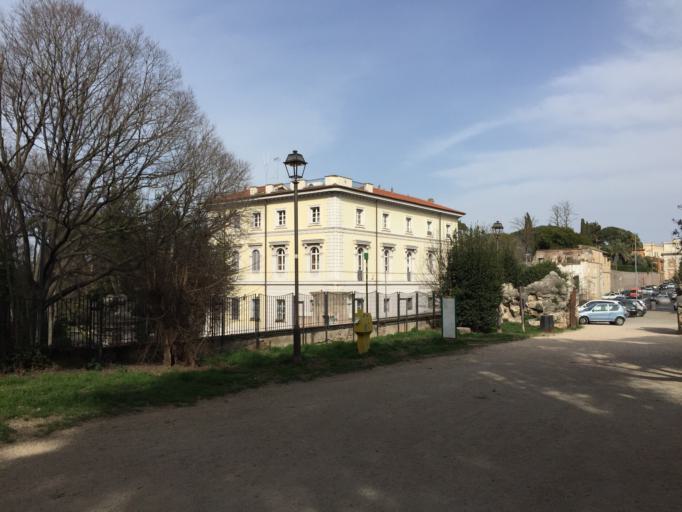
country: VA
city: Vatican City
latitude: 41.8873
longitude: 12.4582
